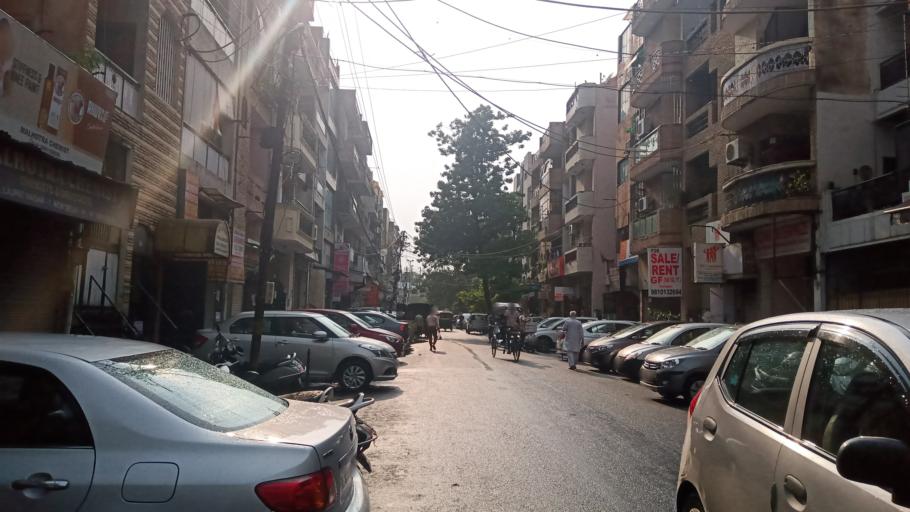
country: IN
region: NCT
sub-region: New Delhi
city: New Delhi
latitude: 28.5743
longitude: 77.2406
